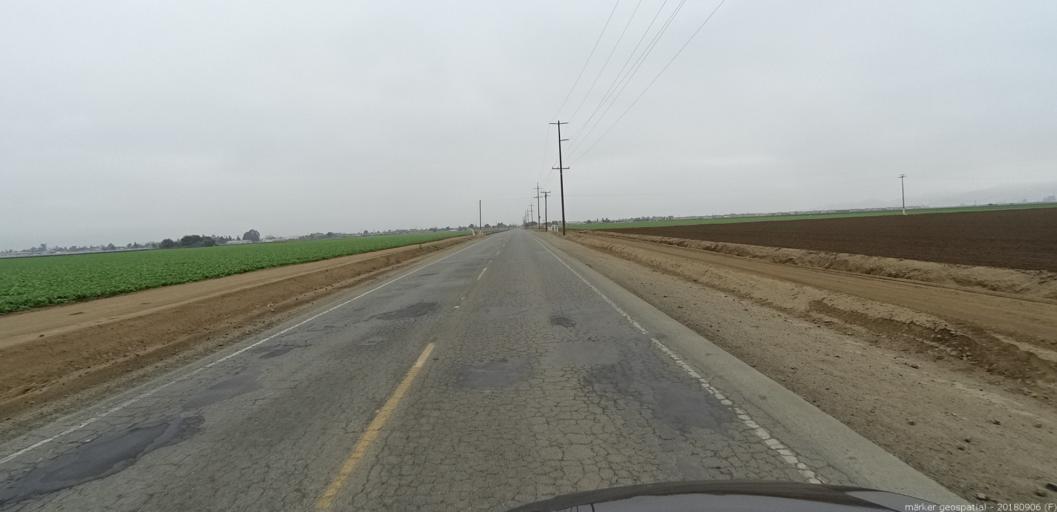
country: US
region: California
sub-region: Monterey County
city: Salinas
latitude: 36.6643
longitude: -121.5936
